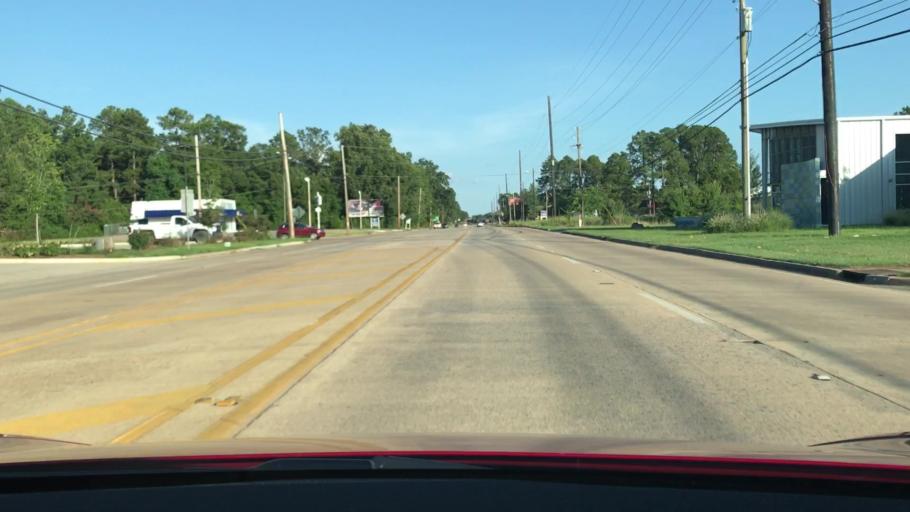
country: US
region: Louisiana
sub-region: Bossier Parish
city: Bossier City
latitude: 32.4279
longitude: -93.7424
